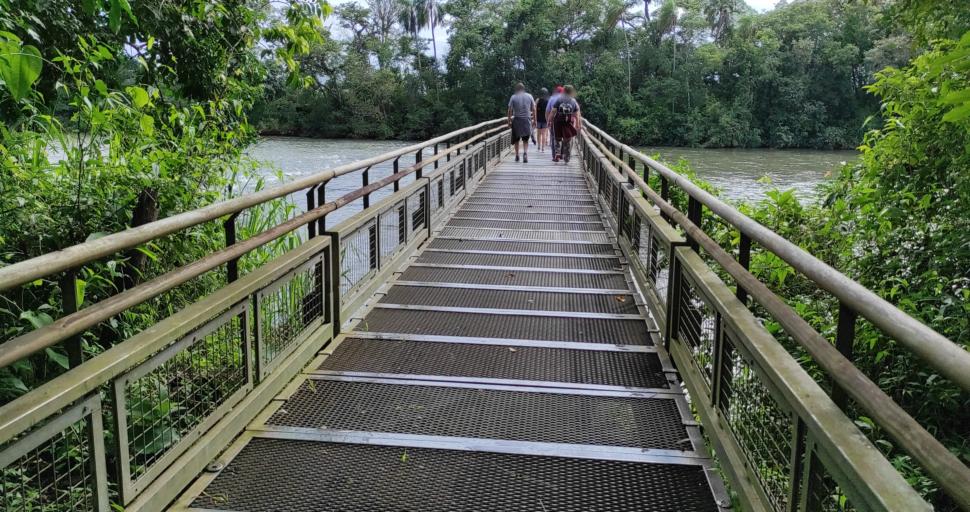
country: AR
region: Misiones
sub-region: Departamento de Iguazu
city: Puerto Iguazu
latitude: -25.6995
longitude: -54.4426
